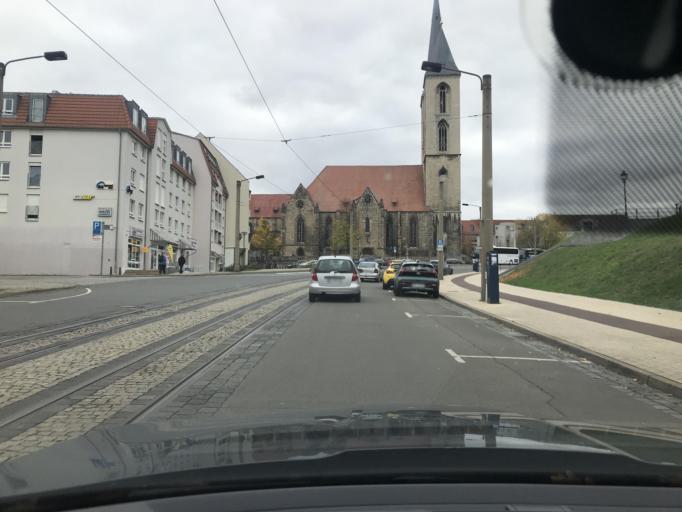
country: DE
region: Saxony-Anhalt
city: Halberstadt
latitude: 51.8969
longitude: 11.0506
